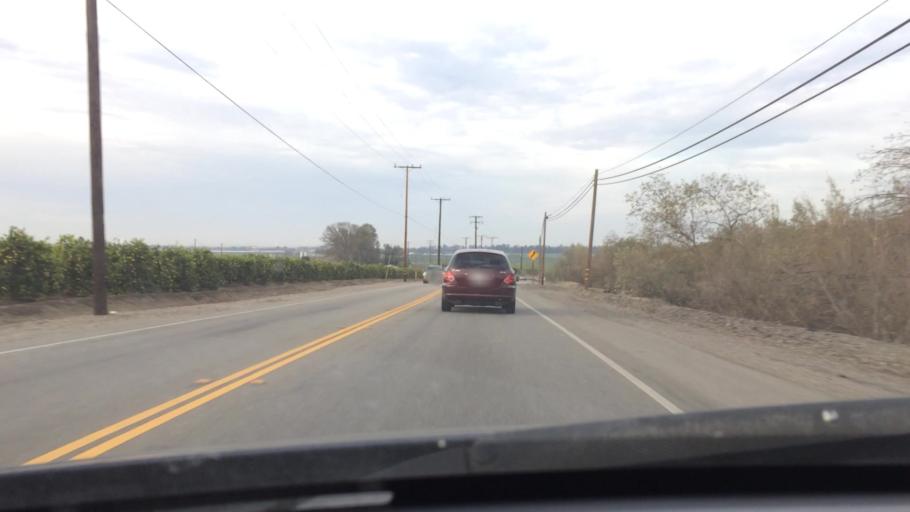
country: US
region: California
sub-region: Ventura County
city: Saticoy
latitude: 34.2601
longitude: -119.1038
